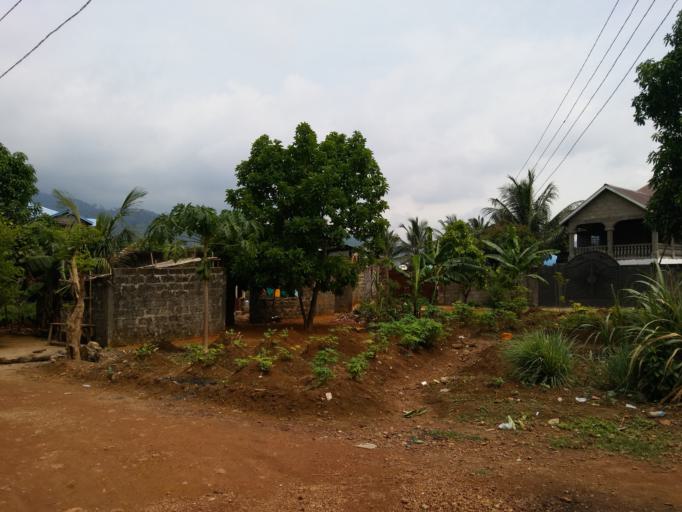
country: SL
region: Western Area
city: Hastings
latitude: 8.3839
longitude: -13.1486
